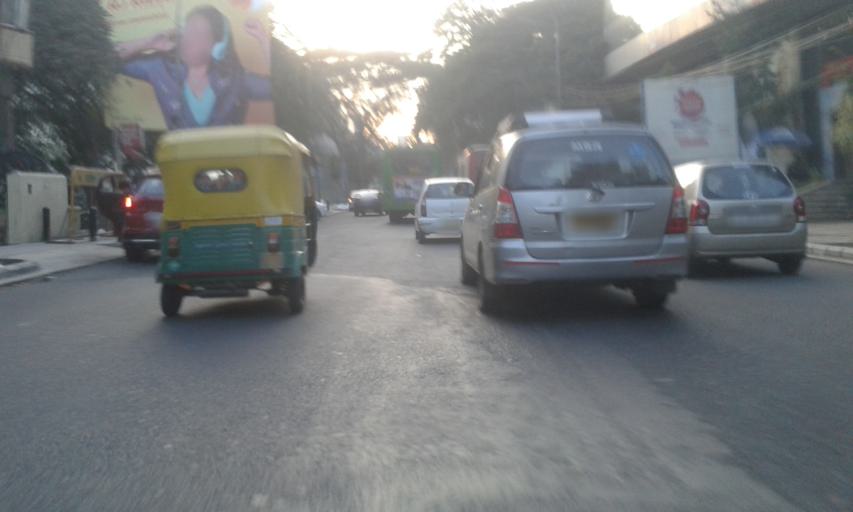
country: IN
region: Karnataka
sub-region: Bangalore Urban
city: Bangalore
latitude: 12.9654
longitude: 77.6014
